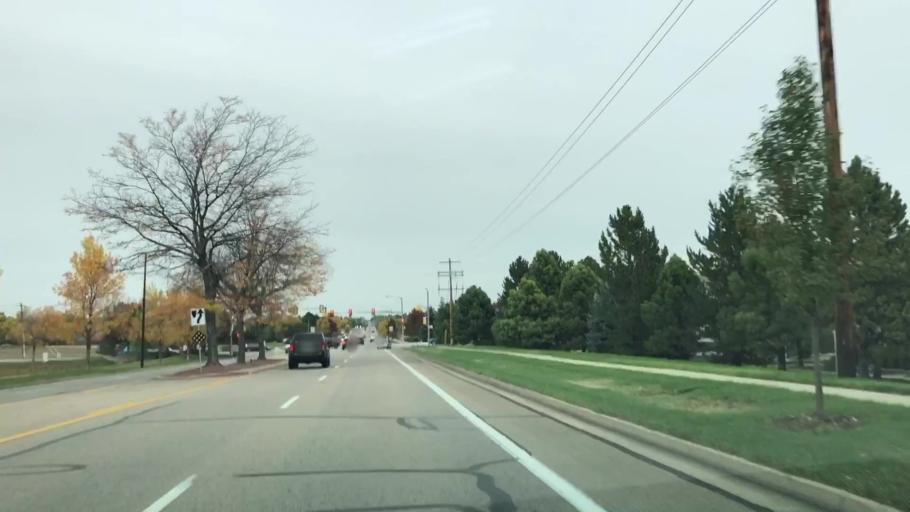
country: US
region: Colorado
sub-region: Larimer County
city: Fort Collins
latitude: 40.4933
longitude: -105.0582
